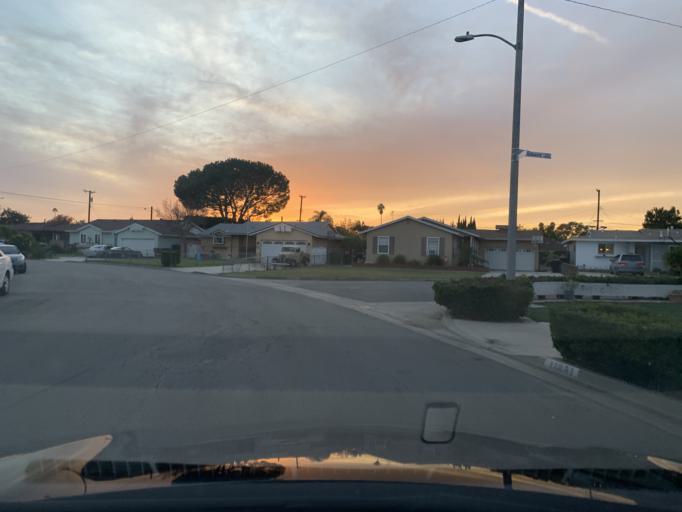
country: US
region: California
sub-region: Orange County
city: Garden Grove
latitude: 33.7898
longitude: -117.9261
